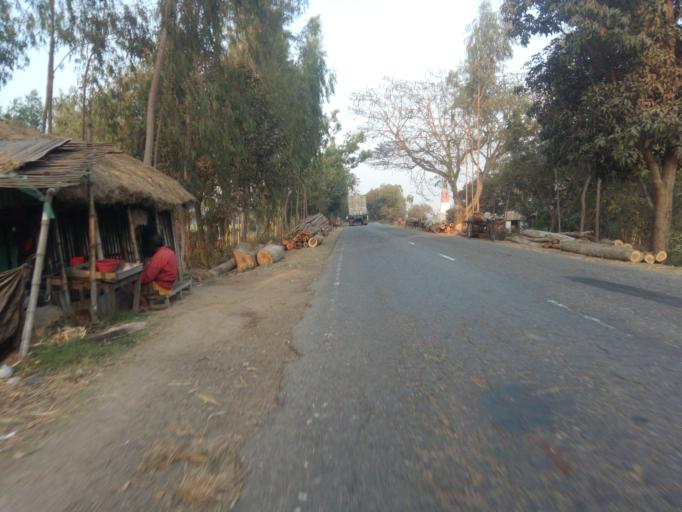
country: BD
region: Rajshahi
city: Bogra
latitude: 24.5572
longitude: 89.1985
